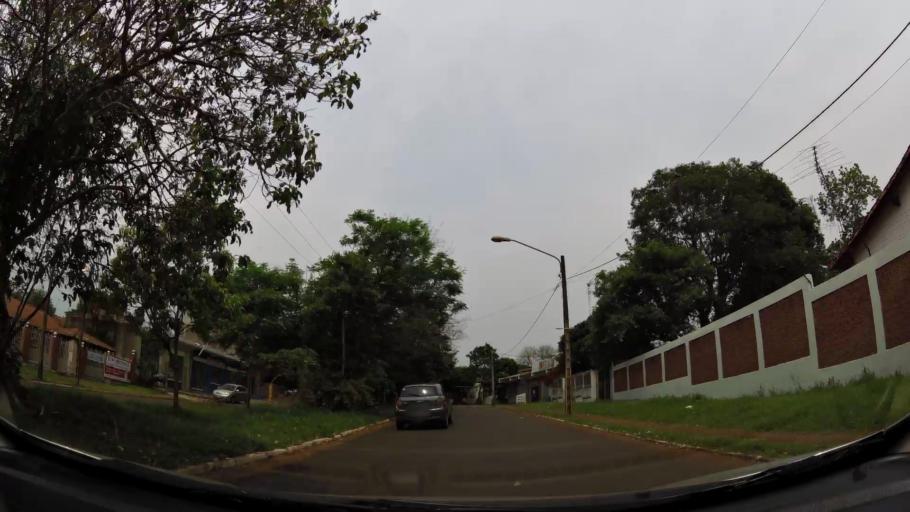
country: PY
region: Alto Parana
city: Presidente Franco
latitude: -25.5505
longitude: -54.6182
